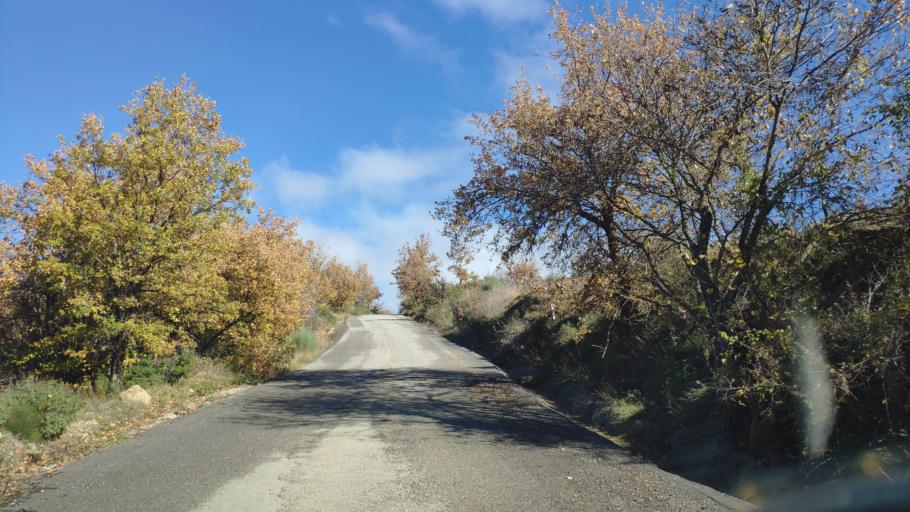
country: GR
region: West Greece
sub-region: Nomos Achaias
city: Aiyira
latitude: 38.0646
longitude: 22.4636
